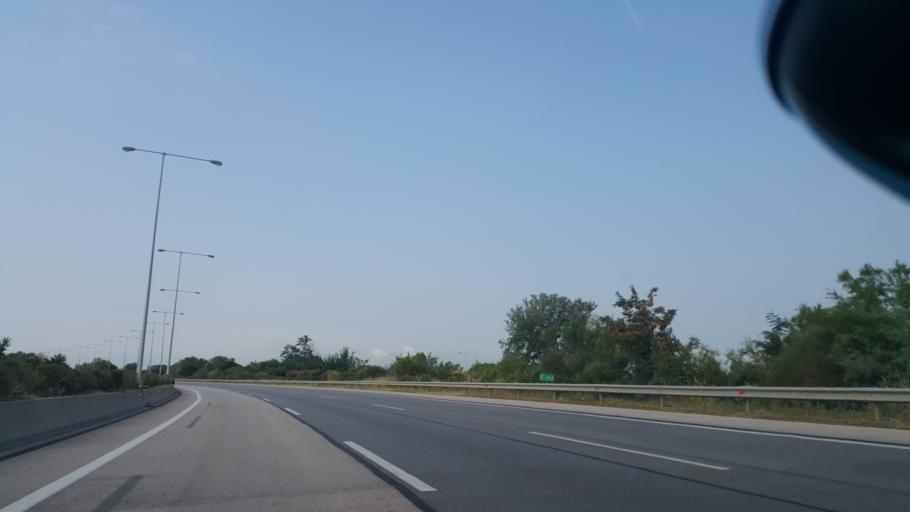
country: GR
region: Central Macedonia
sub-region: Nomos Thessalonikis
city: Nea Magnisia
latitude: 40.6865
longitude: 22.8335
